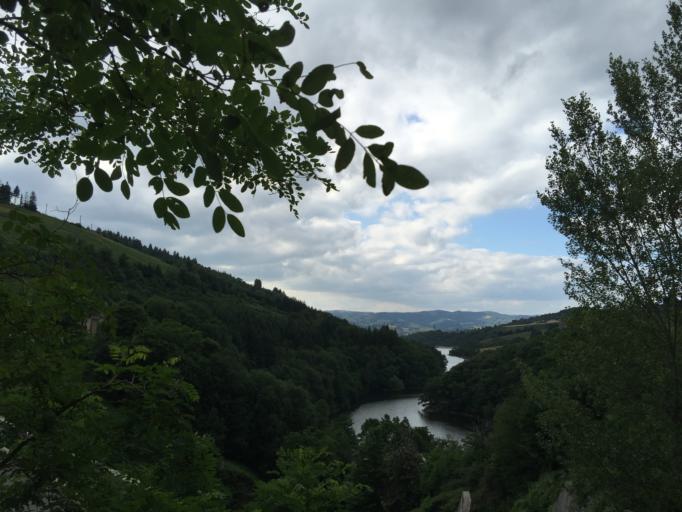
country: FR
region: Rhone-Alpes
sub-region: Departement de la Loire
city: Saint-Chamond
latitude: 45.4256
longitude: 4.5165
